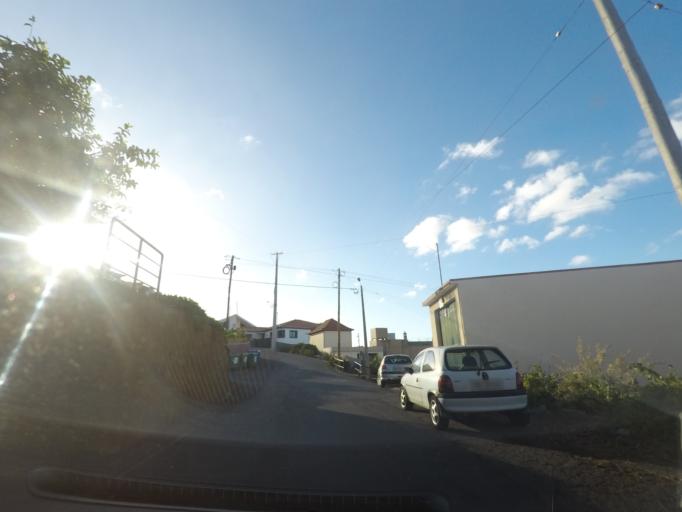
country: PT
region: Madeira
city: Ponta do Sol
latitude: 32.6883
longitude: -17.0897
